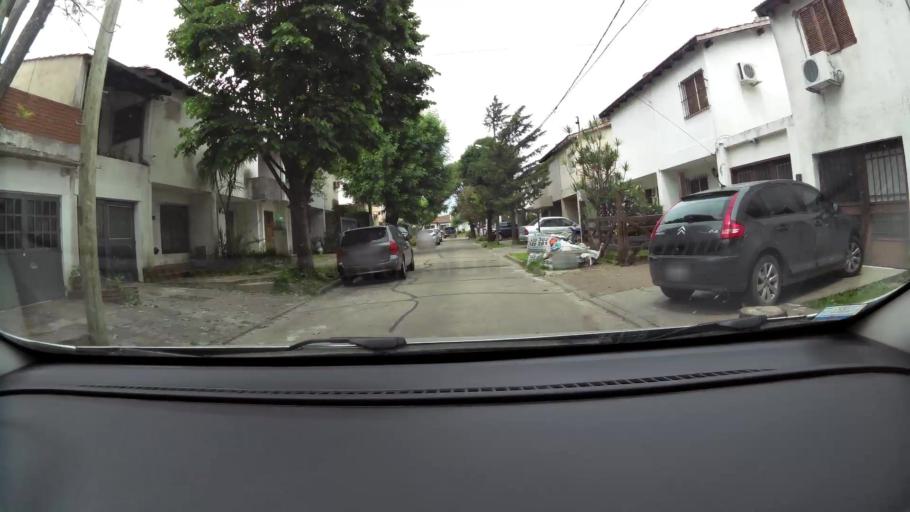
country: AR
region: Buenos Aires
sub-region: Partido de Campana
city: Campana
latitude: -34.1764
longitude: -58.9693
